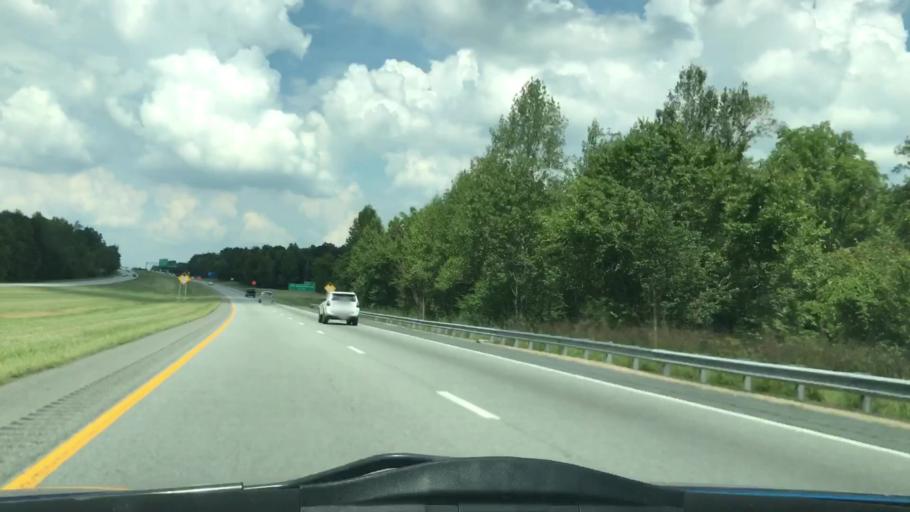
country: US
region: North Carolina
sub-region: Guilford County
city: Pleasant Garden
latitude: 35.9758
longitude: -79.8213
